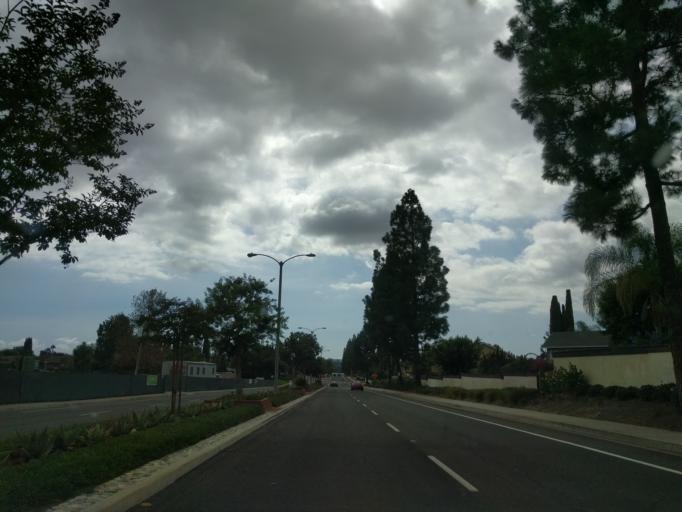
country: US
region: California
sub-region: Orange County
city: Laguna Hills
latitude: 33.6273
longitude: -117.7071
